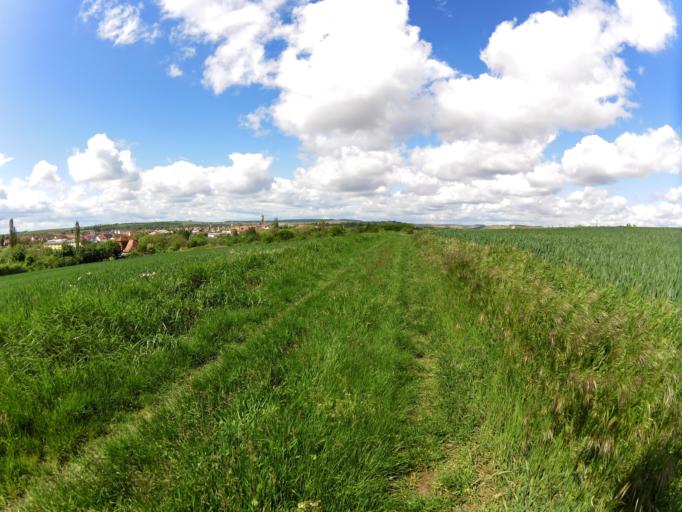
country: DE
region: Bavaria
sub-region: Regierungsbezirk Unterfranken
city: Volkach
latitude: 49.8693
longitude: 10.2398
